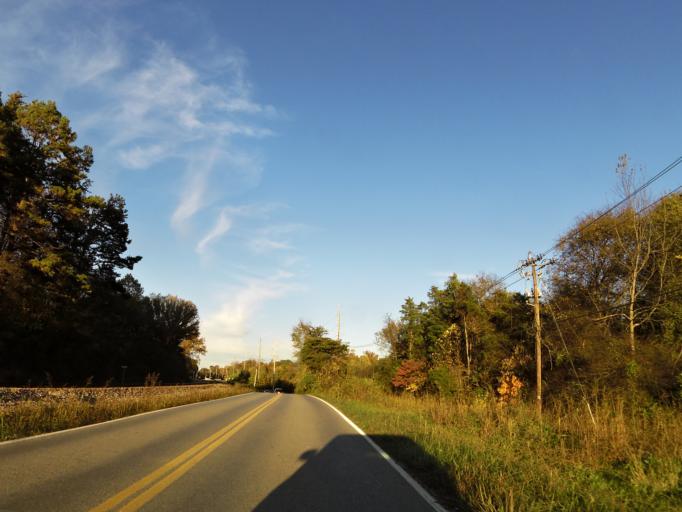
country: US
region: Tennessee
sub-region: Blount County
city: Louisville
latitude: 35.9002
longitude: -84.0535
